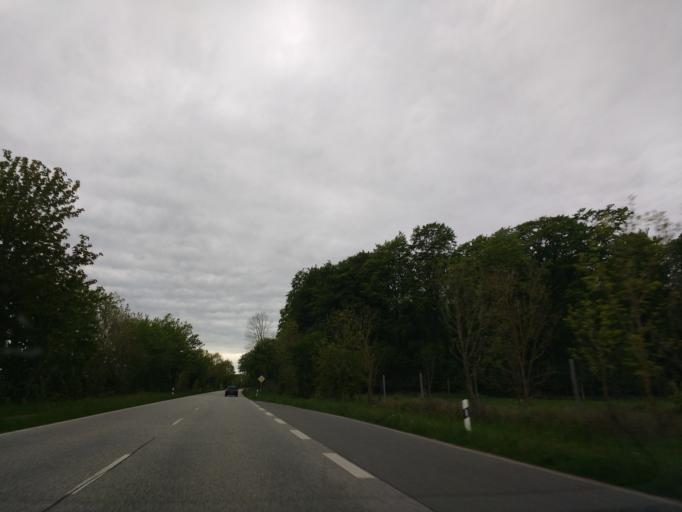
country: DE
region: Schleswig-Holstein
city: Damp
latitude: 54.5943
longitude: 9.9656
